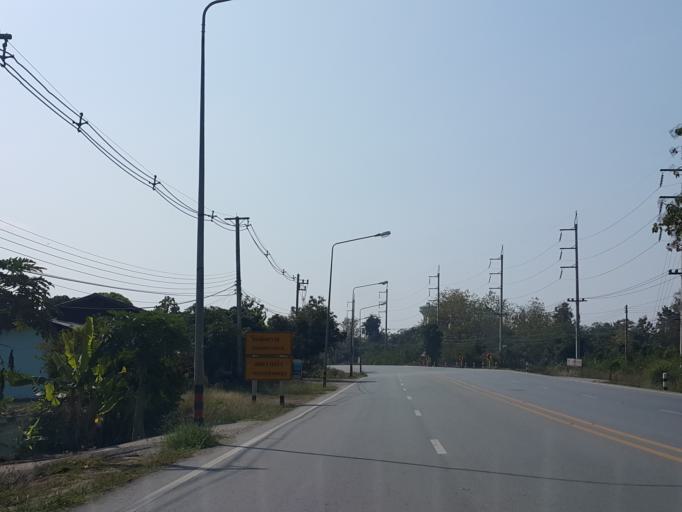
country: TH
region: Chiang Mai
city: Chom Thong
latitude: 18.3226
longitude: 98.6648
